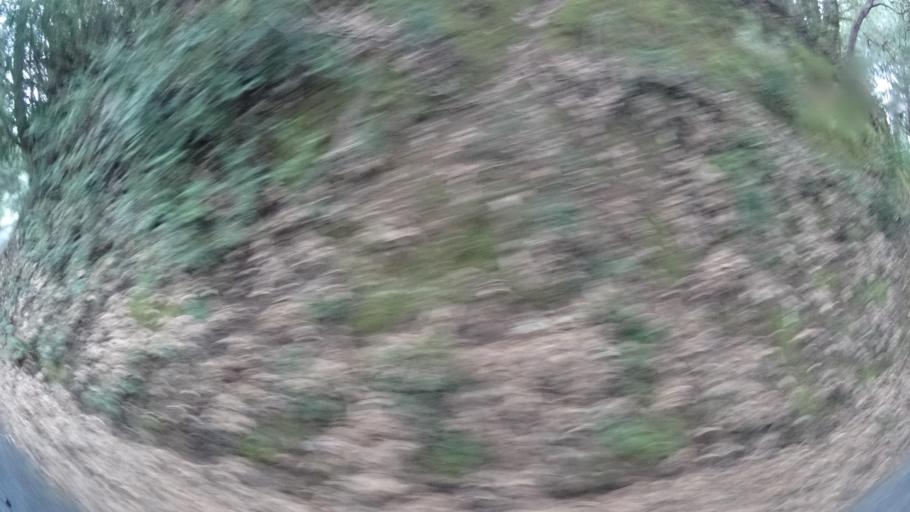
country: US
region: California
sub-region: Humboldt County
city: Redway
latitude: 40.2740
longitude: -123.7711
